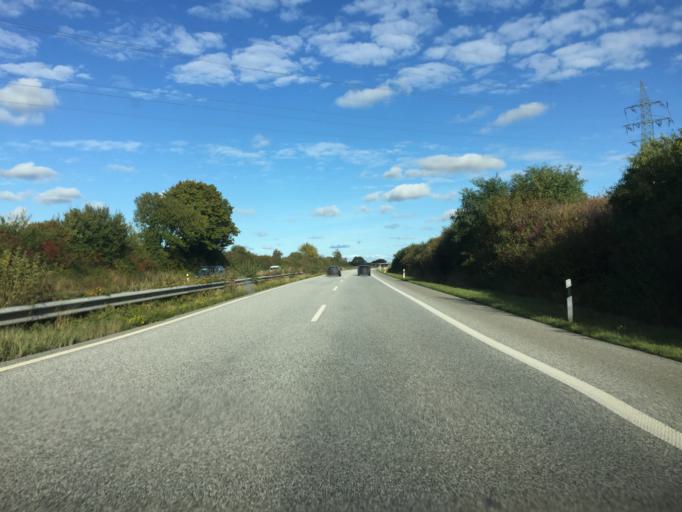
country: DE
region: Schleswig-Holstein
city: Damlos
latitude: 54.2537
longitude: 10.8879
